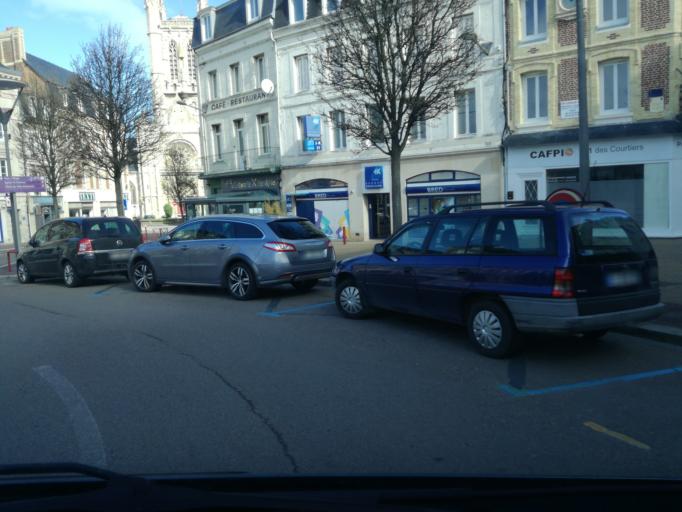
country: FR
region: Haute-Normandie
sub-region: Departement de la Seine-Maritime
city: Fecamp
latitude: 49.7572
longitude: 0.3765
